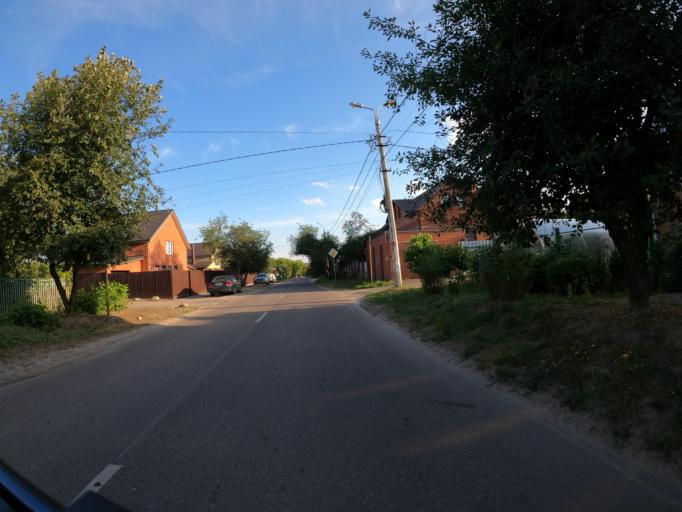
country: RU
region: Moskovskaya
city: Raduzhnyy
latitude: 55.1068
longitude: 38.7275
